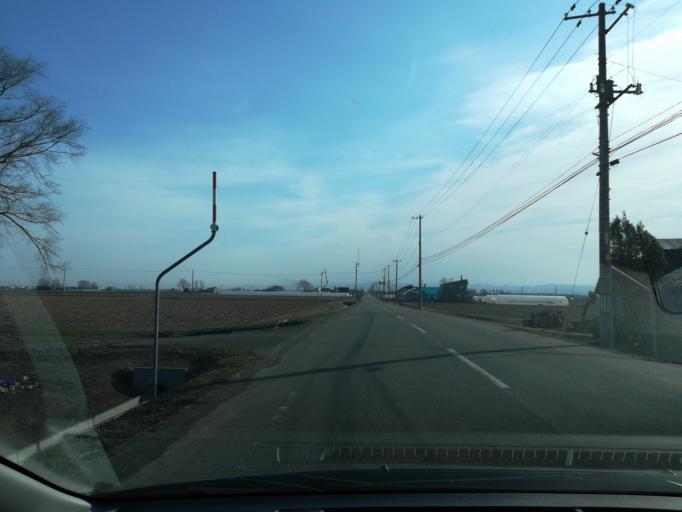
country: JP
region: Hokkaido
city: Iwamizawa
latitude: 43.1650
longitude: 141.6574
